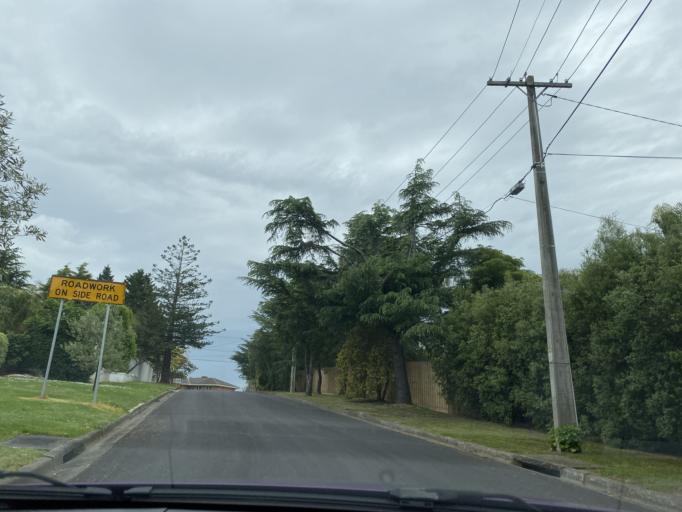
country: AU
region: Victoria
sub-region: Manningham
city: Templestowe Lower
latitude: -37.7655
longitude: 145.1393
